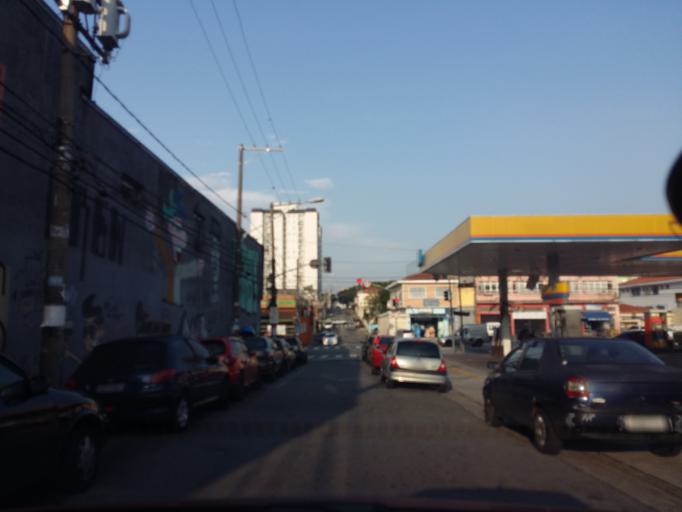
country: BR
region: Sao Paulo
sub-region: Diadema
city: Diadema
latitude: -23.6344
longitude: -46.6164
